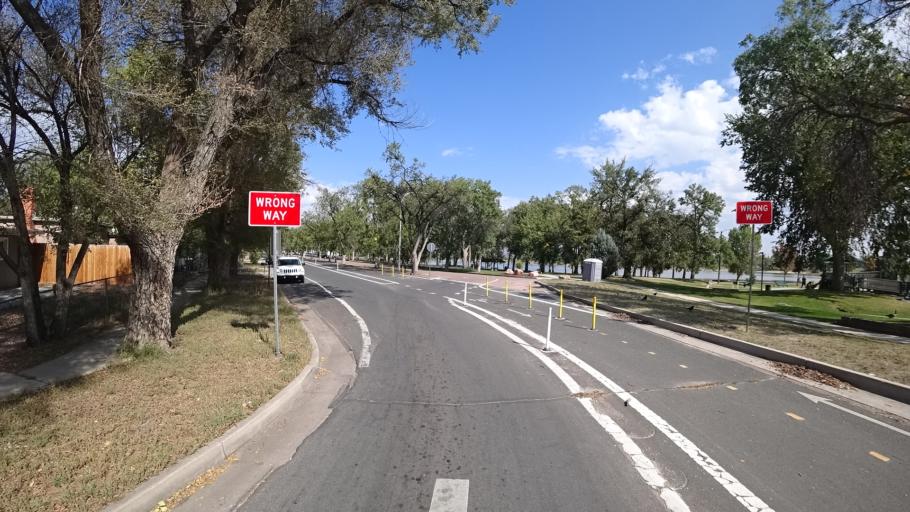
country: US
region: Colorado
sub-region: El Paso County
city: Colorado Springs
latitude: 38.8226
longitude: -104.7999
